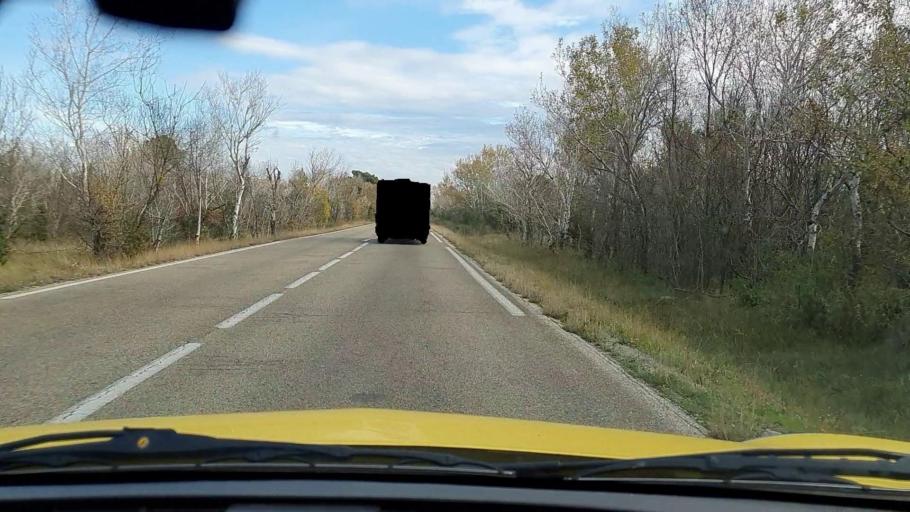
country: FR
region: Languedoc-Roussillon
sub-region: Departement du Gard
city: Aramon
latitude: 43.9059
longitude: 4.7113
